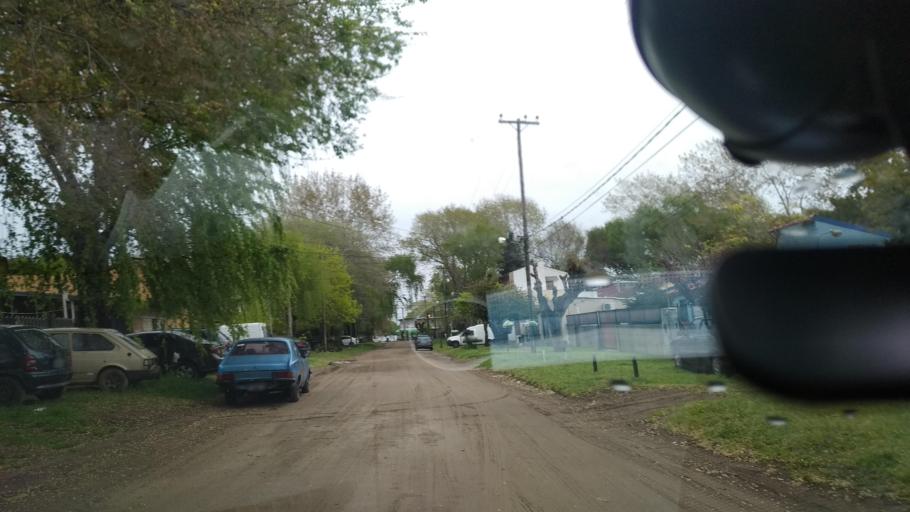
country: AR
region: Buenos Aires
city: Mar del Tuyu
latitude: -36.5321
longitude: -56.7114
